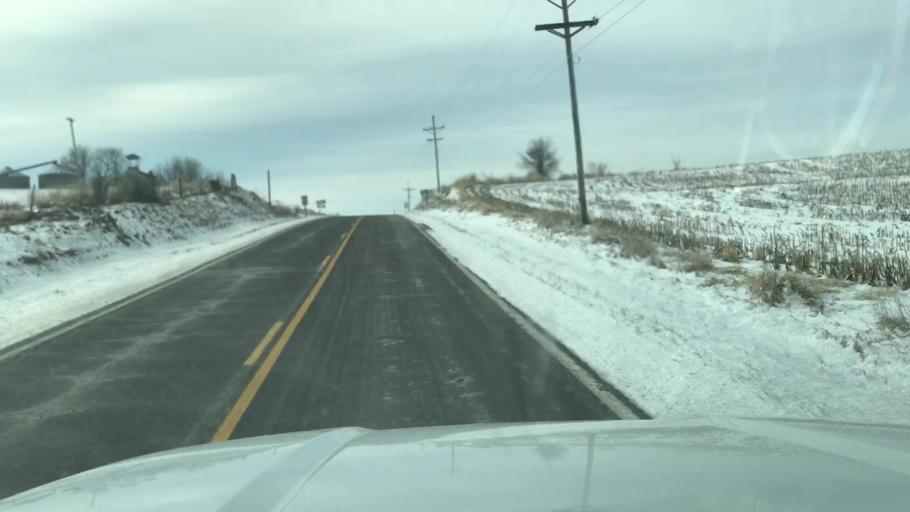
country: US
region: Missouri
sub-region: Holt County
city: Oregon
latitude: 40.0658
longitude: -95.1356
